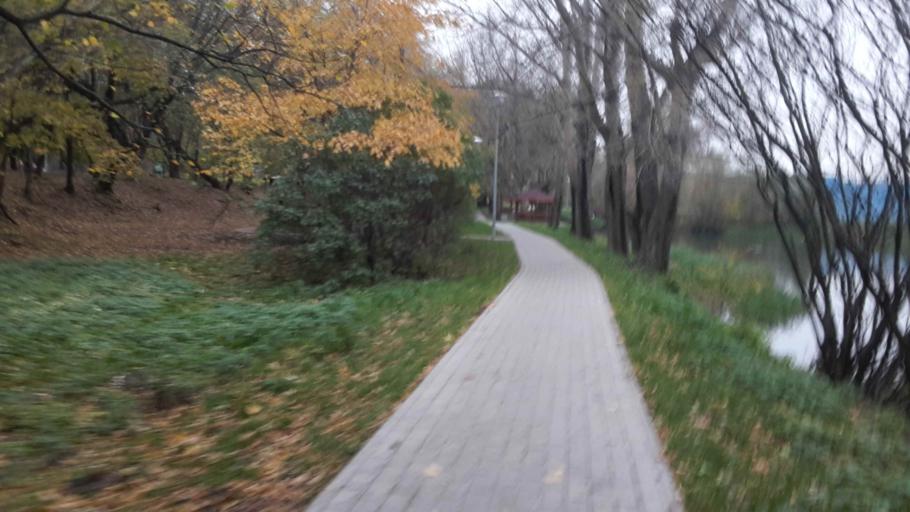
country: RU
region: Moscow
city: Orekhovo-Borisovo
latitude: 55.6311
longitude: 37.7326
